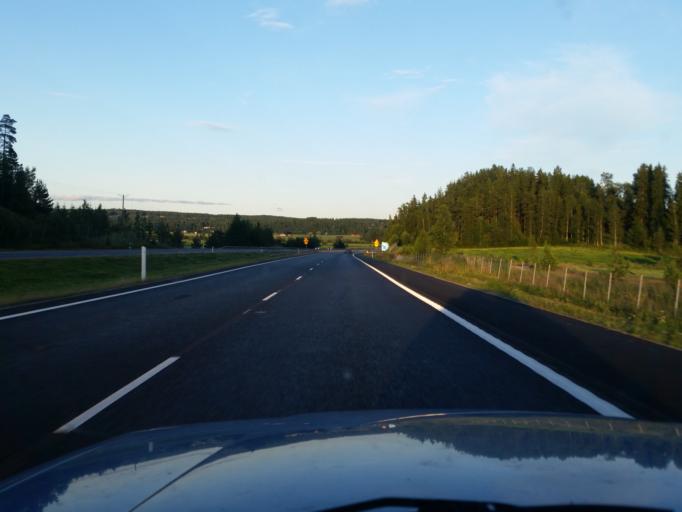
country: FI
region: Varsinais-Suomi
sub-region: Turku
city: Paimio
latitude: 60.4360
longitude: 22.6388
